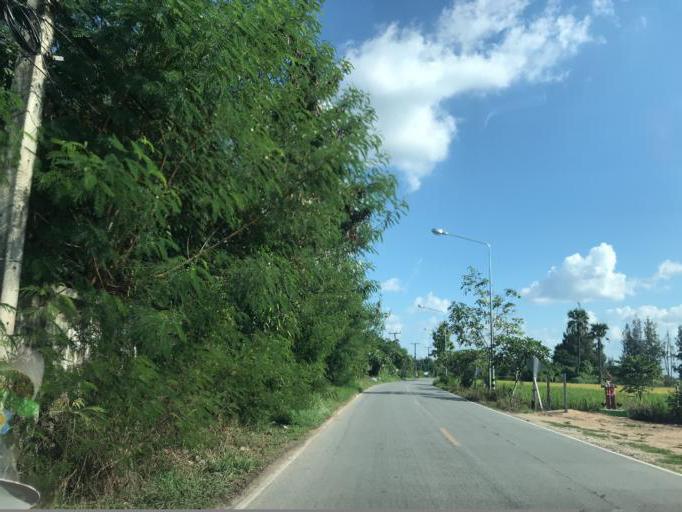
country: TH
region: Chiang Mai
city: Doi Lo
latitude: 18.5352
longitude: 98.8410
